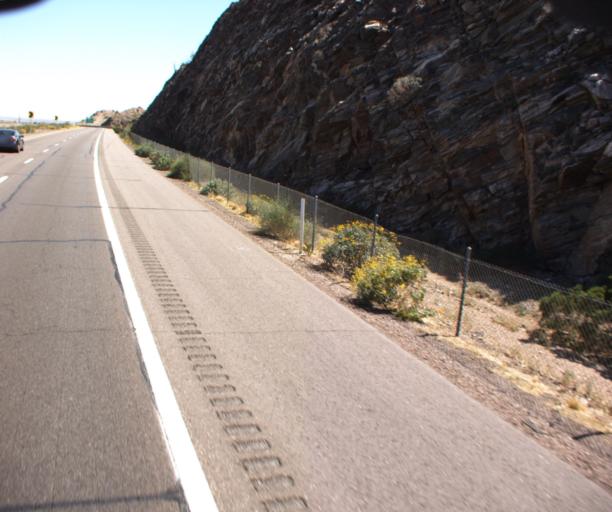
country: US
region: Arizona
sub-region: Yuma County
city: Wellton
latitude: 32.7257
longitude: -113.7485
